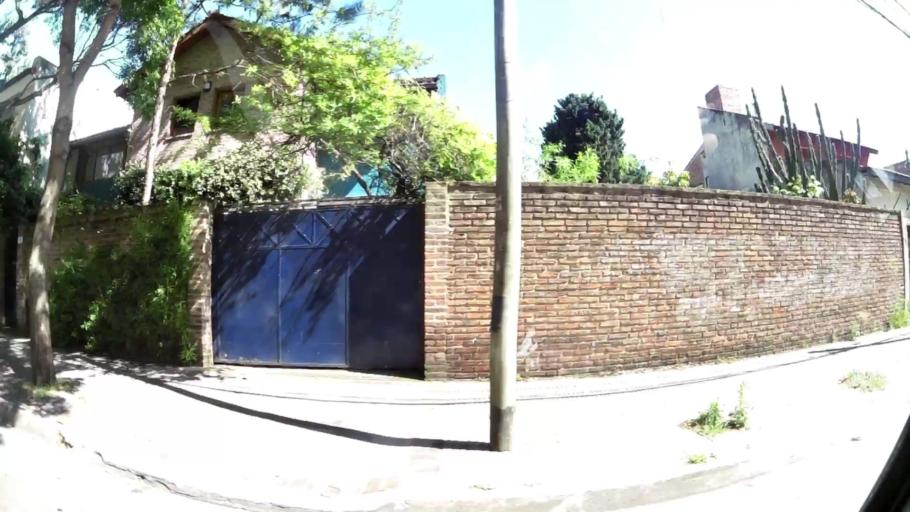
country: AR
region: Buenos Aires
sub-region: Partido de Vicente Lopez
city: Olivos
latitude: -34.5206
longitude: -58.4769
